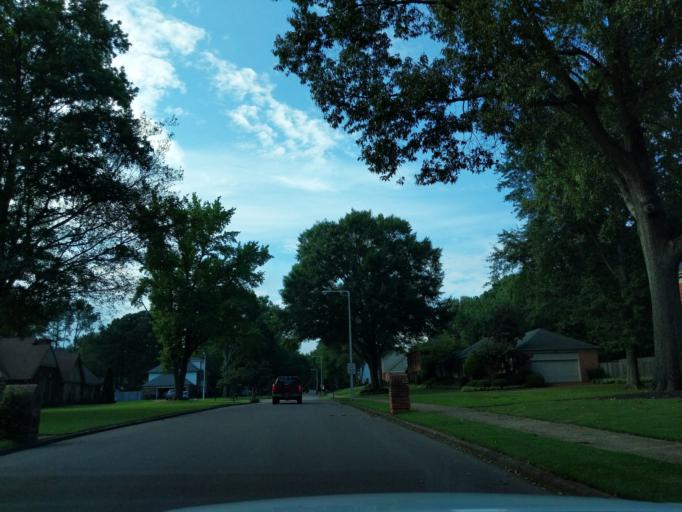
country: US
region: Tennessee
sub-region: Shelby County
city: Germantown
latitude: 35.0667
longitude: -89.7845
